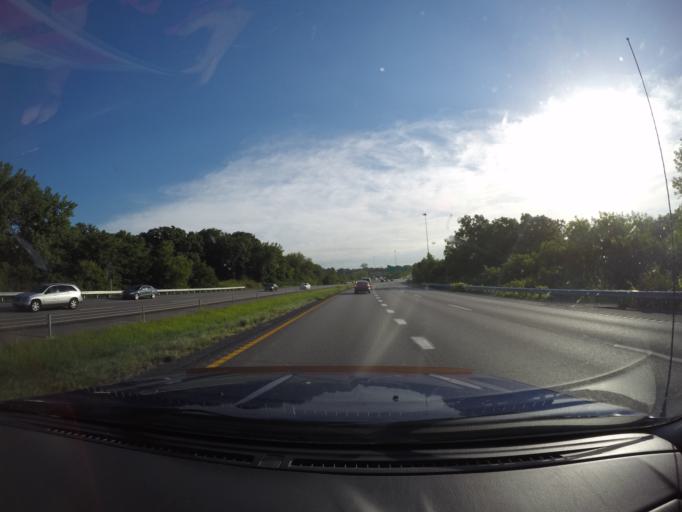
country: US
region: Missouri
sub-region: Platte County
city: Riverside
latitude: 39.1869
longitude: -94.6202
